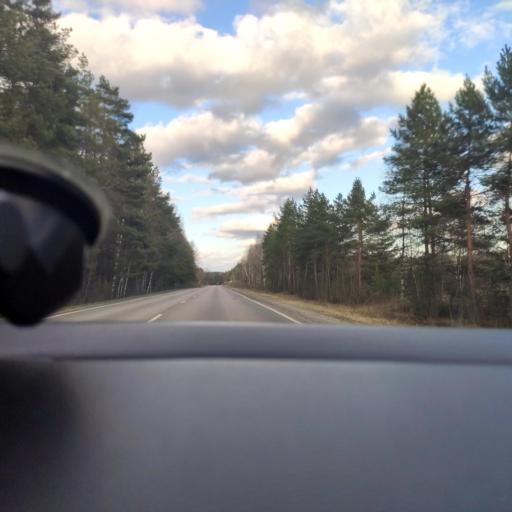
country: RU
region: Moskovskaya
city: Shaturtorf
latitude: 55.4283
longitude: 39.3394
